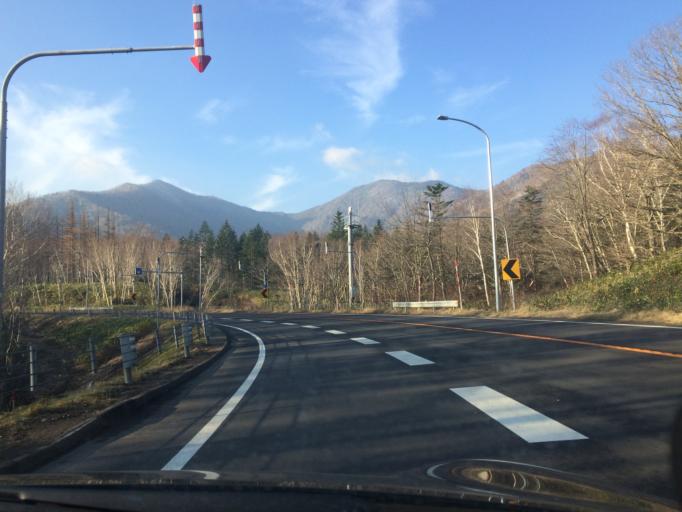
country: JP
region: Hokkaido
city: Otofuke
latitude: 42.9605
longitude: 142.7931
